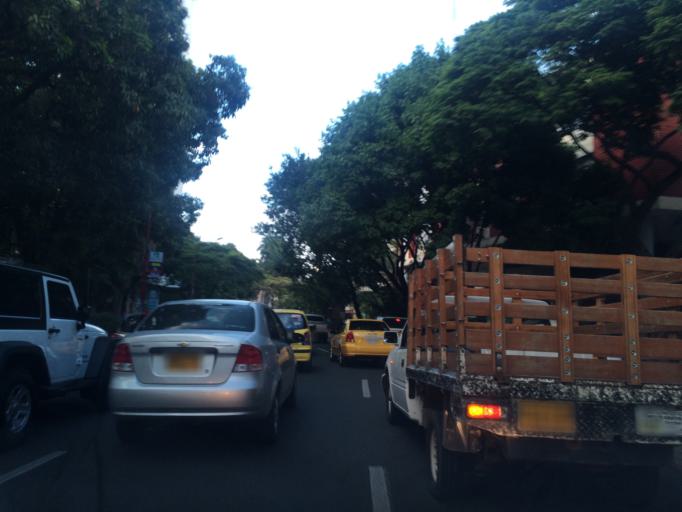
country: CO
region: Valle del Cauca
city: Cali
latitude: 3.4614
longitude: -76.5309
